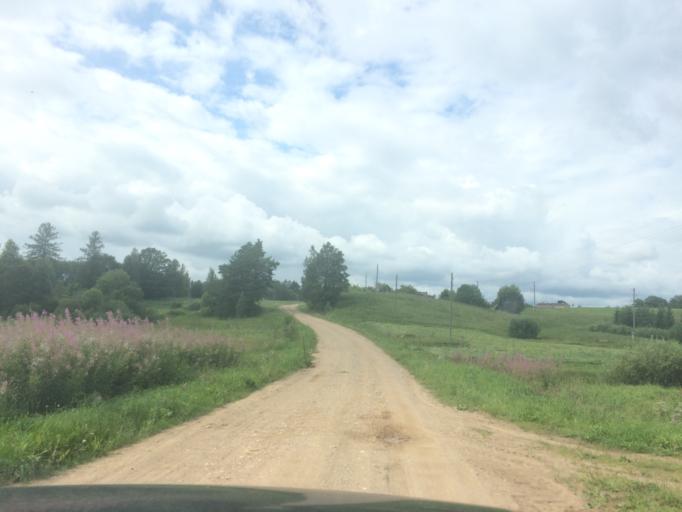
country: LV
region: Rezekne
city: Rezekne
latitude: 56.6577
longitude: 27.2725
